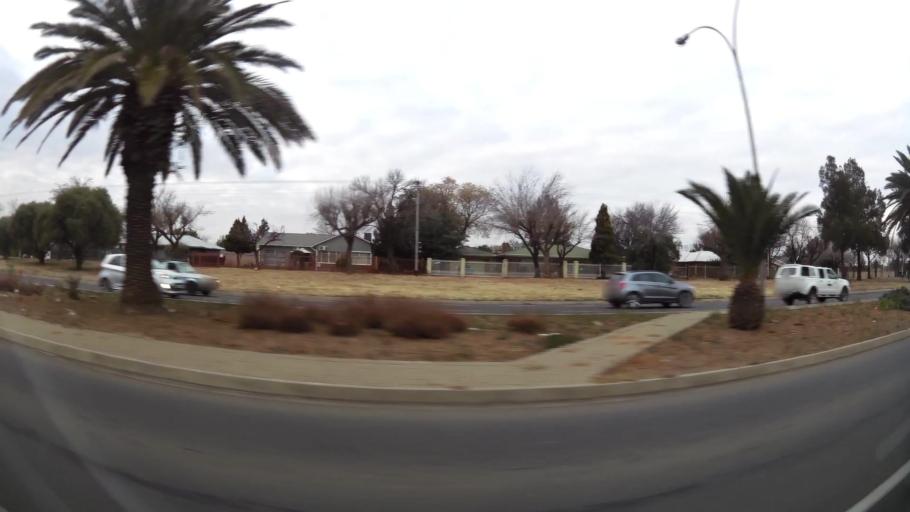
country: ZA
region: Orange Free State
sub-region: Mangaung Metropolitan Municipality
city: Bloemfontein
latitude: -29.1266
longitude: 26.1698
